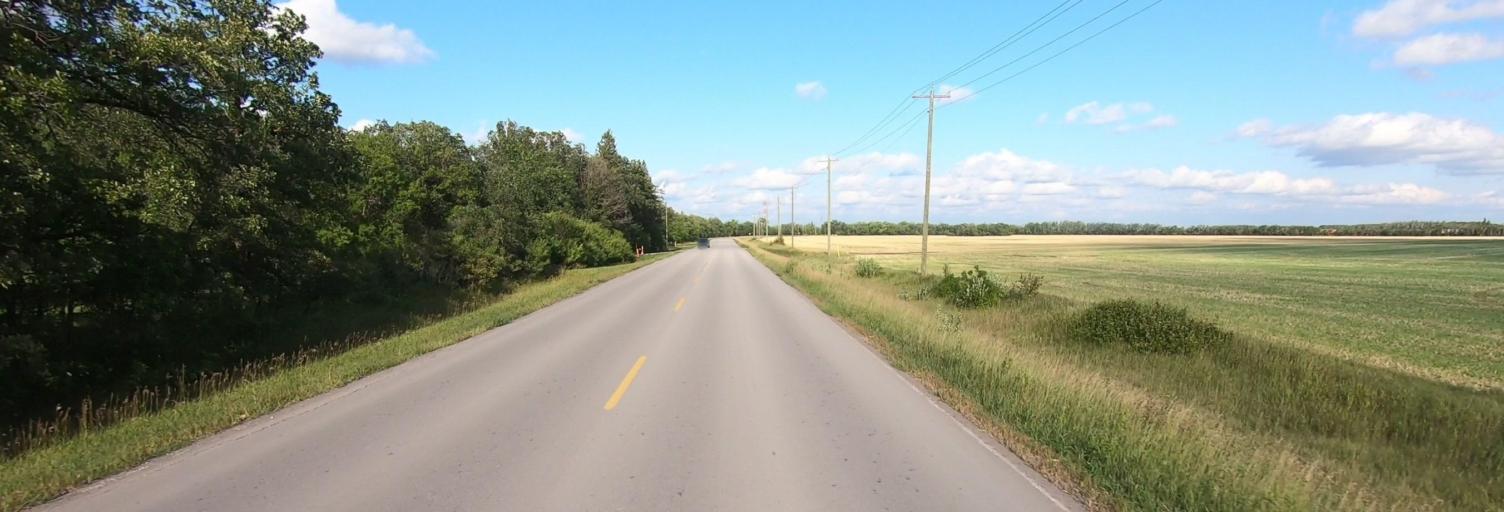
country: CA
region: Manitoba
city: Selkirk
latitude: 50.1204
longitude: -96.8770
